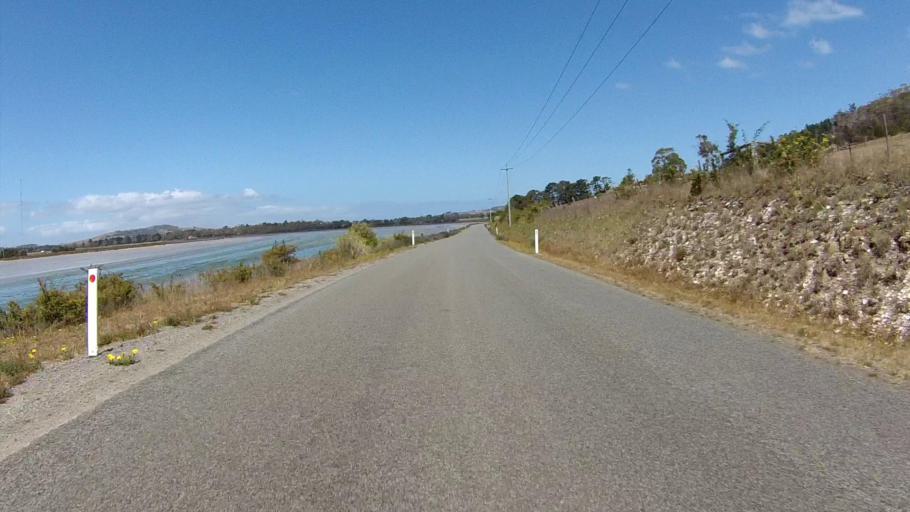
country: AU
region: Tasmania
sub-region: Clarence
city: Lauderdale
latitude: -42.9203
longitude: 147.4793
